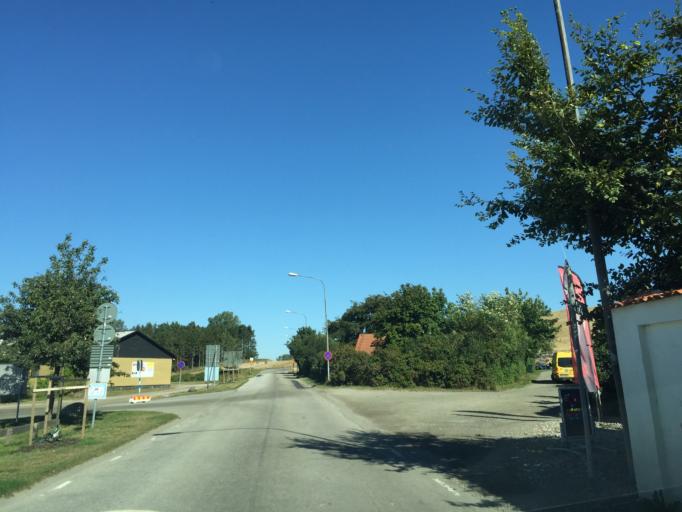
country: SE
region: Skane
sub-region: Ystads Kommun
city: Kopingebro
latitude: 55.3884
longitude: 14.0637
